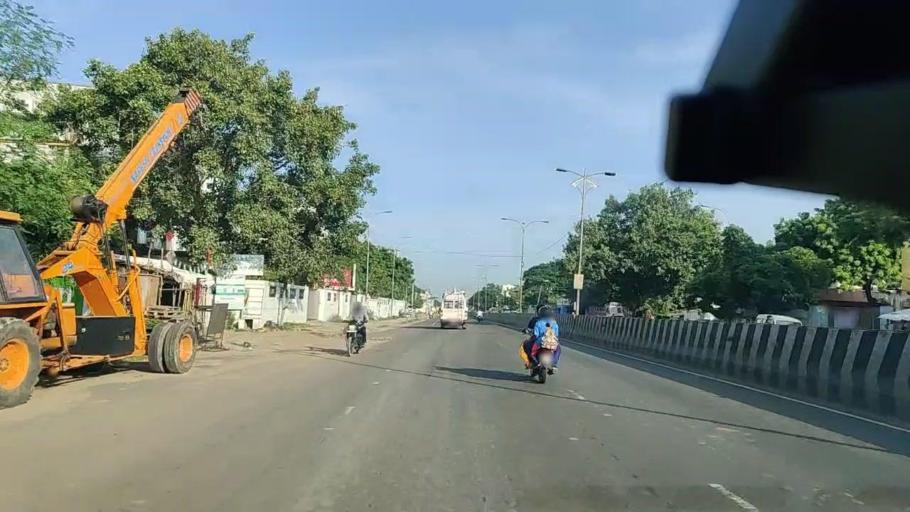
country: IN
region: Tamil Nadu
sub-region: Thiruvallur
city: Chinnasekkadu
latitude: 13.1383
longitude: 80.2285
